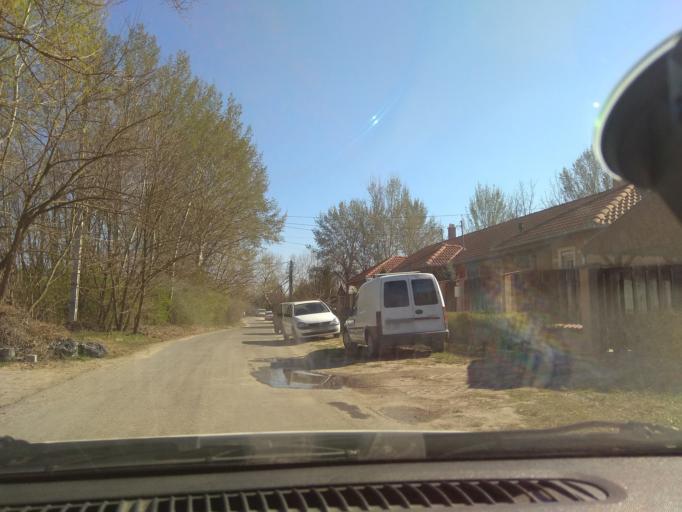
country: HU
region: Pest
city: Szigethalom
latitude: 47.3262
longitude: 19.0248
